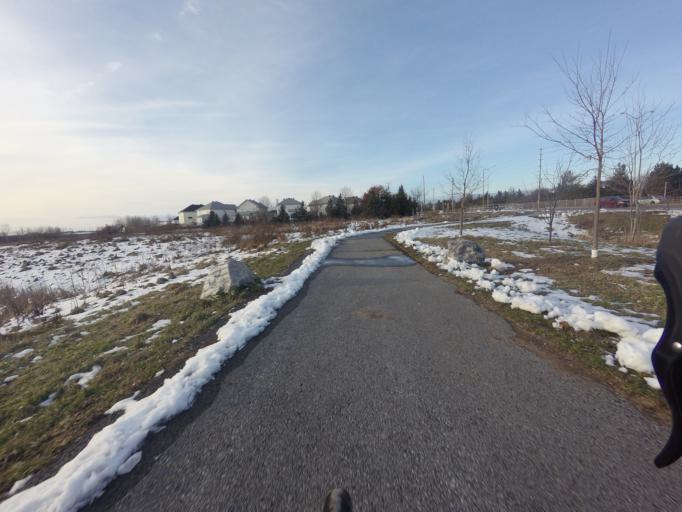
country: CA
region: Ontario
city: Bells Corners
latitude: 45.2887
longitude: -75.8908
